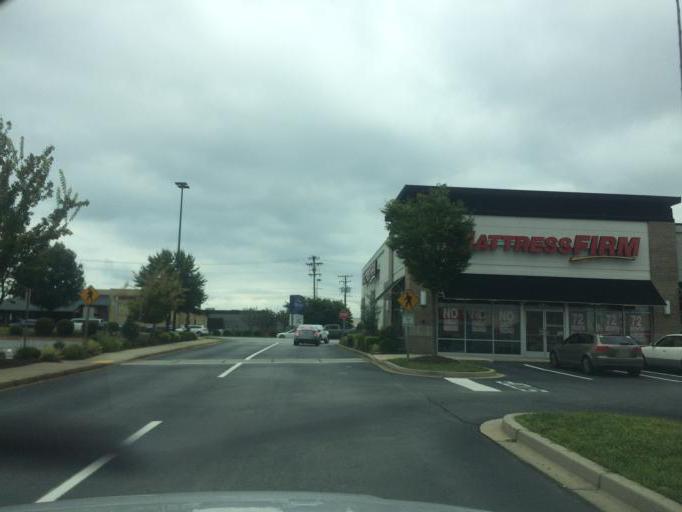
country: US
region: South Carolina
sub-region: Greenville County
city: Mauldin
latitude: 34.8297
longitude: -82.3054
